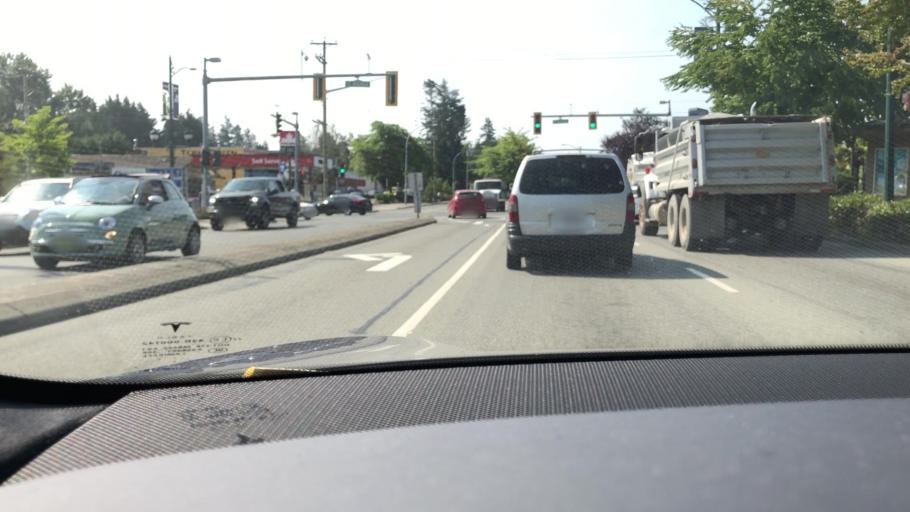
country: US
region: Washington
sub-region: Whatcom County
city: Point Roberts
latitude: 49.0252
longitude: -123.0688
